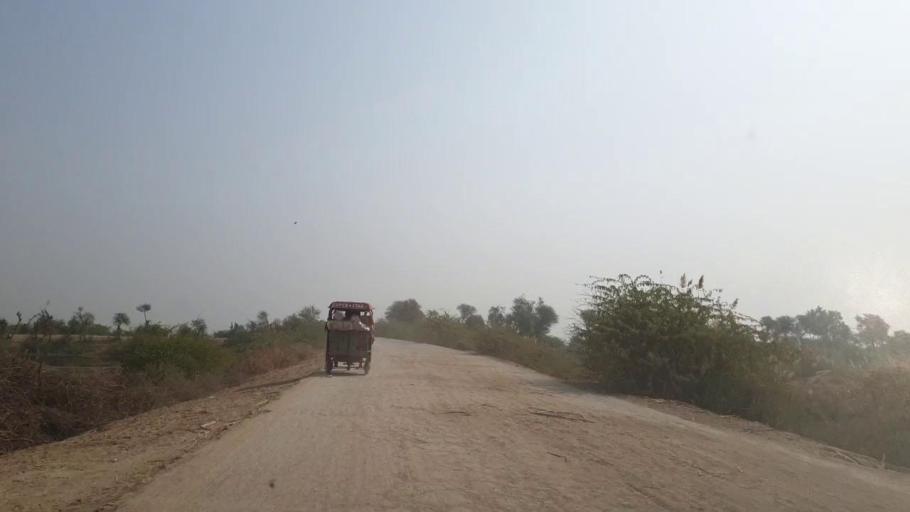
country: PK
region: Sindh
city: Mirpur Khas
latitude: 25.5561
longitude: 69.0943
